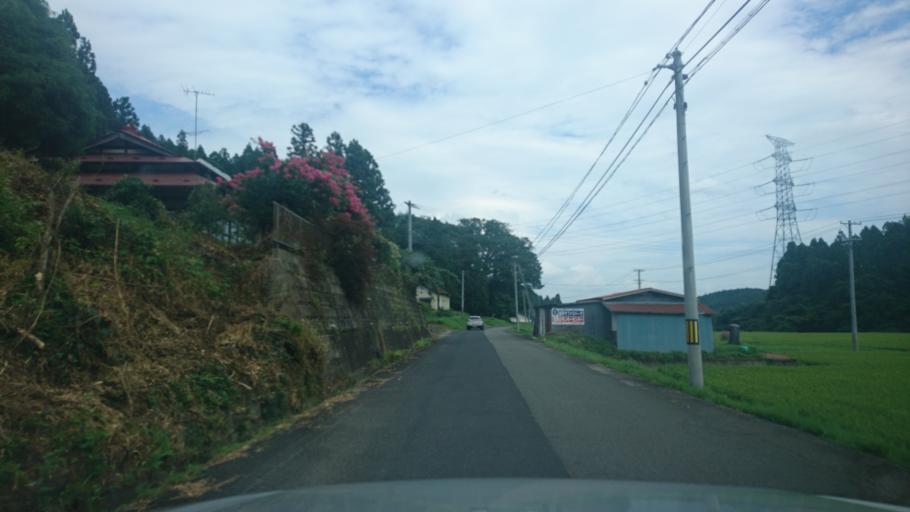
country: JP
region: Miyagi
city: Furukawa
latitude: 38.7729
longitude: 140.9235
